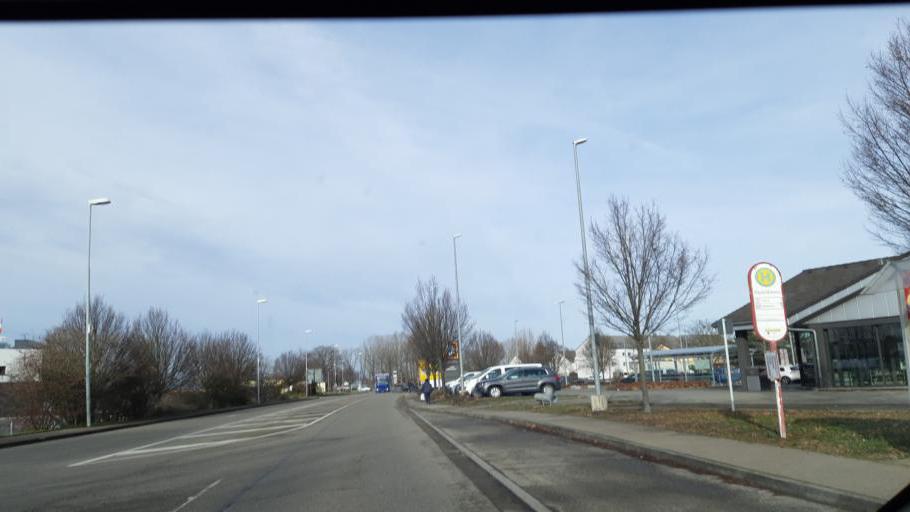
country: DE
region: Baden-Wuerttemberg
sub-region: Freiburg Region
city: Herbolzheim
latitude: 48.2238
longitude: 7.7636
